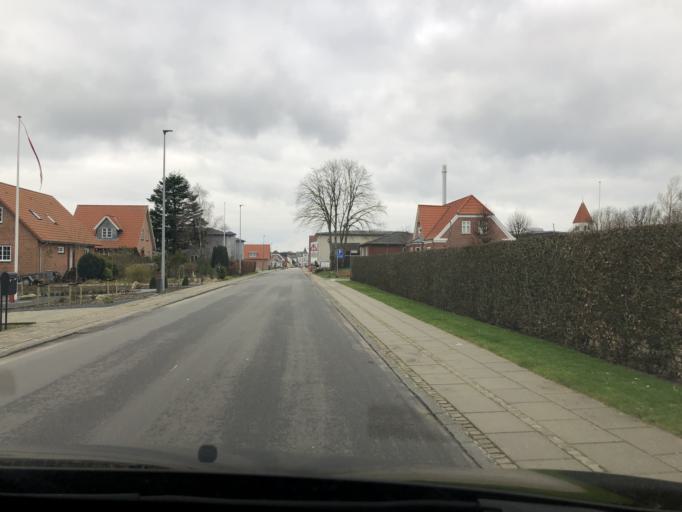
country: DK
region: Central Jutland
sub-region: Ringkobing-Skjern Kommune
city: Tarm
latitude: 55.9047
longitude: 8.5256
